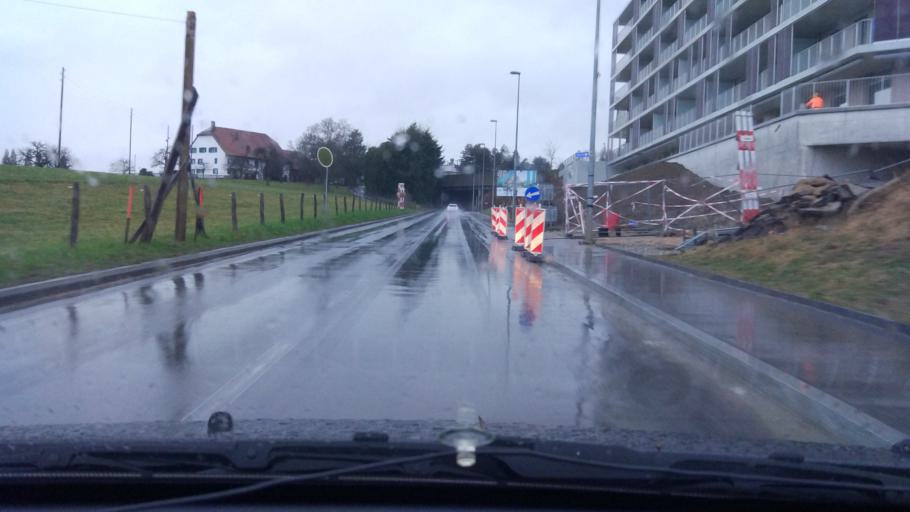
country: CH
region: Vaud
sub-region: Lausanne District
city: Blecherette
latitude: 46.5457
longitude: 6.6295
